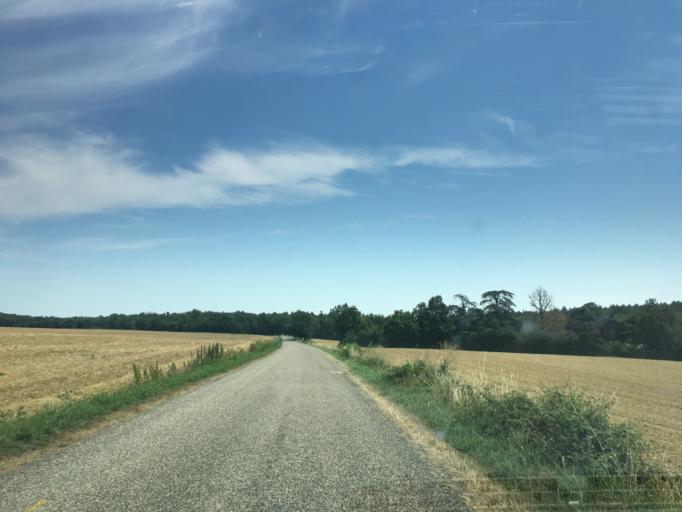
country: FR
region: Midi-Pyrenees
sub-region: Departement du Gers
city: Fleurance
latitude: 43.8170
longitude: 0.5684
